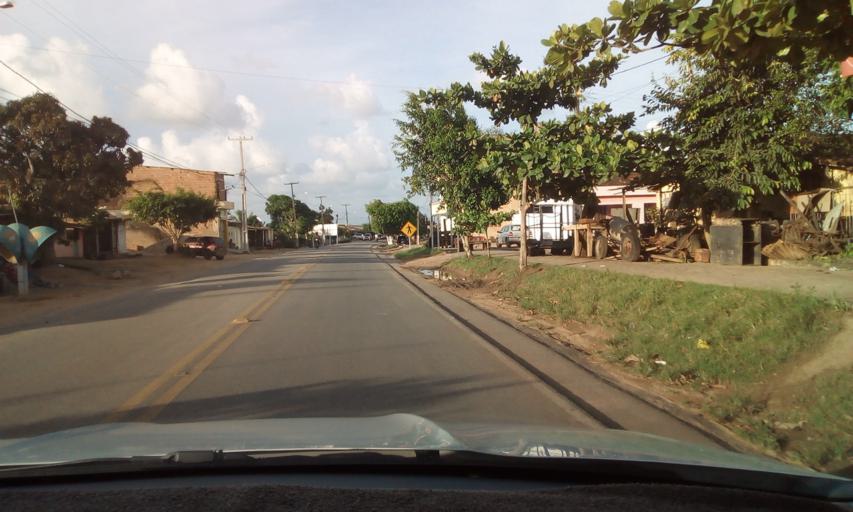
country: BR
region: Pernambuco
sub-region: Gloria Do Goita
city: Gloria do Goita
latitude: -7.9935
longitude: -35.2075
